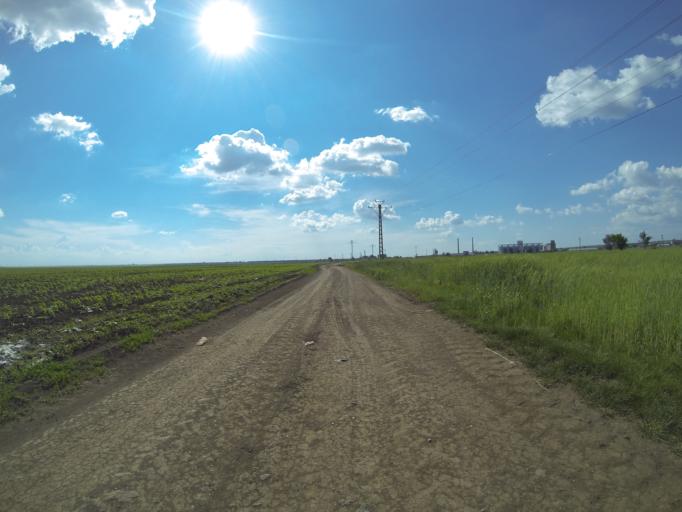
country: RO
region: Dolj
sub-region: Comuna Segarcea
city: Segarcea
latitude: 44.0783
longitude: 23.7384
